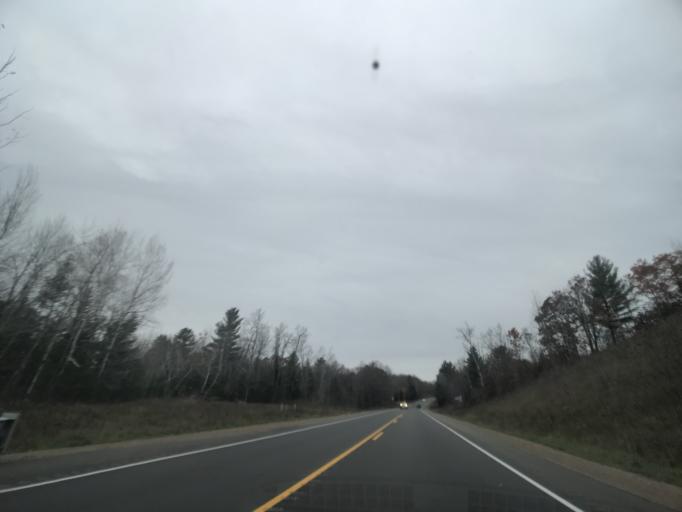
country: US
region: Wisconsin
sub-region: Menominee County
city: Legend Lake
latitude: 45.2748
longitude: -88.5092
